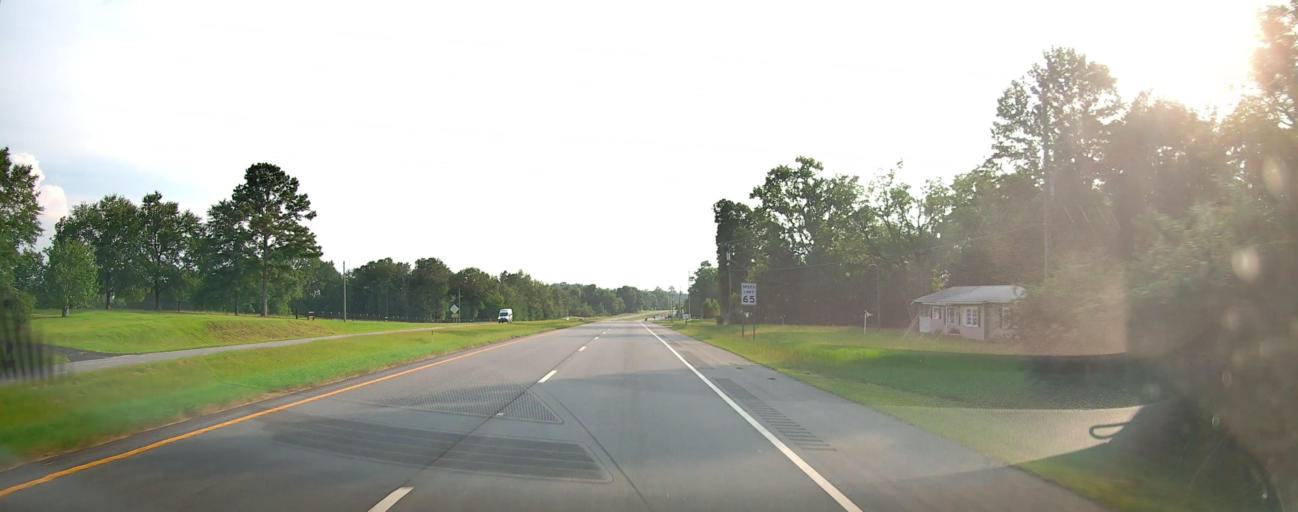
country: US
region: Georgia
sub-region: Talbot County
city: Talbotton
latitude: 32.5591
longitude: -84.6490
